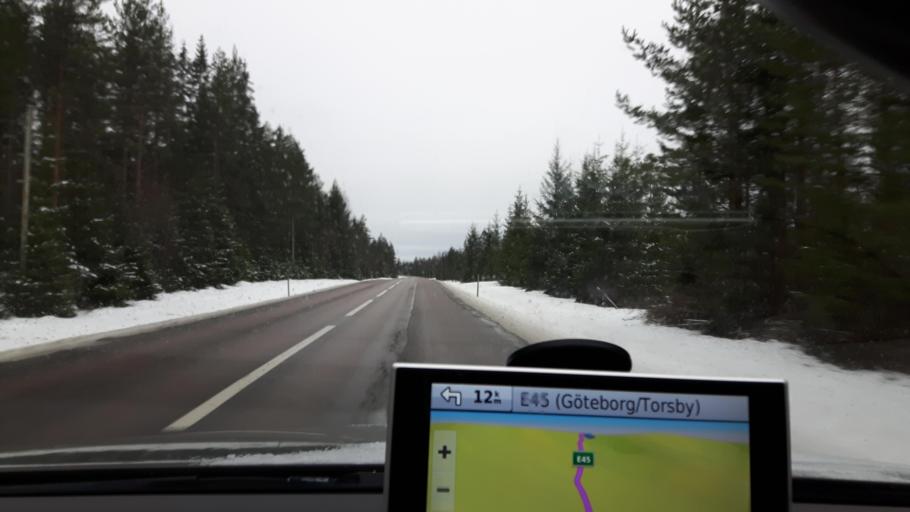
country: SE
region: Vaermland
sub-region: Torsby Kommun
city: Torsby
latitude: 60.3602
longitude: 13.1812
